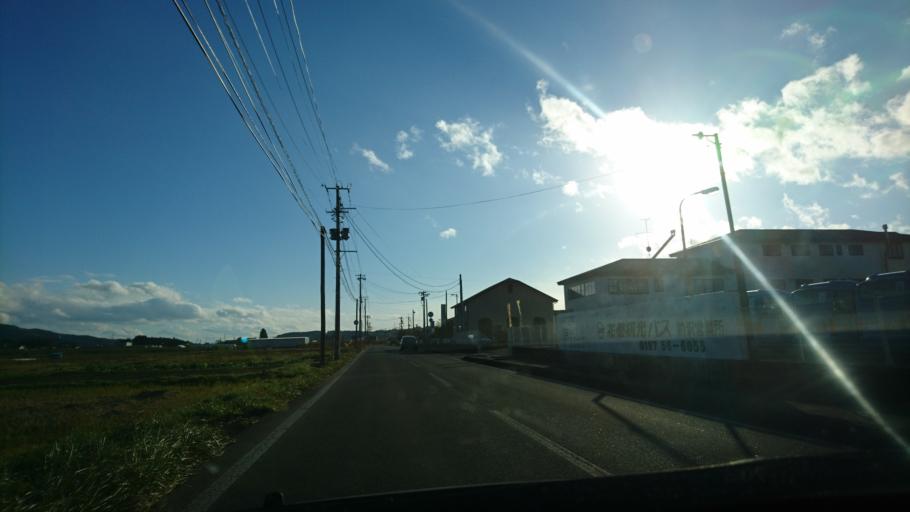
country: JP
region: Iwate
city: Mizusawa
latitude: 39.0503
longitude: 141.1359
